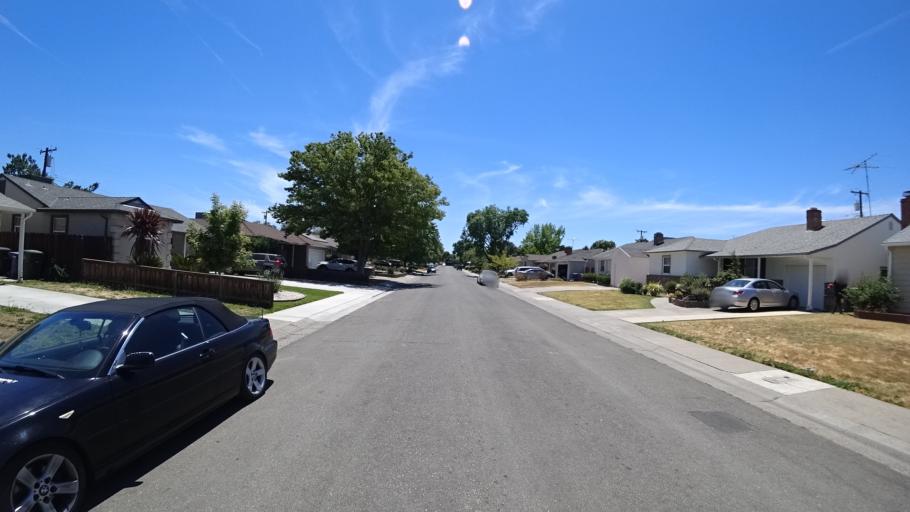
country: US
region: California
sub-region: Sacramento County
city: Parkway
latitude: 38.5243
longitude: -121.4929
